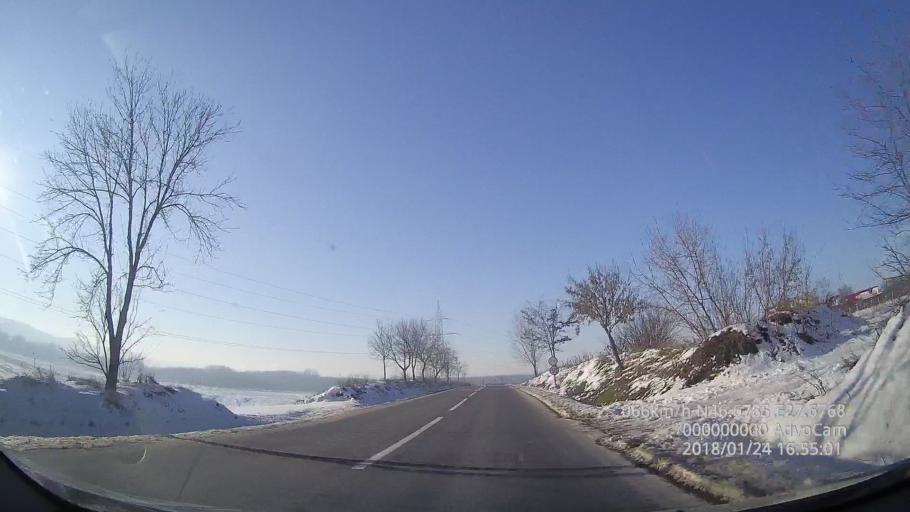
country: RO
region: Vaslui
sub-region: Municipiul Vaslui
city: Brodoc
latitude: 46.6787
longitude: 27.6762
